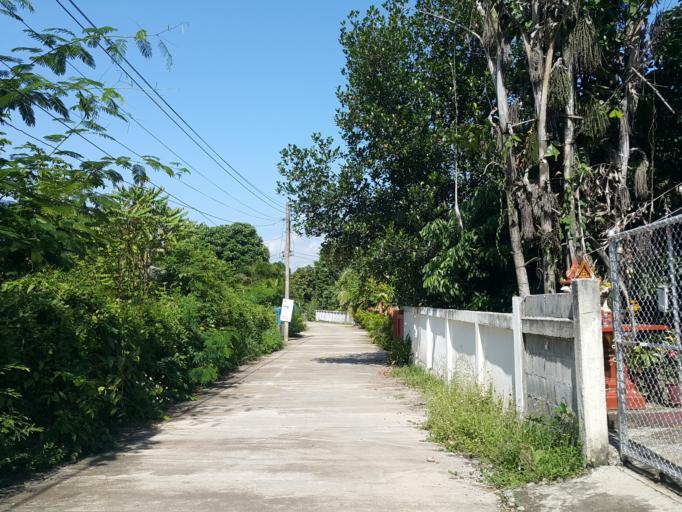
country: TH
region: Chiang Mai
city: San Kamphaeng
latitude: 18.7665
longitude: 99.1746
